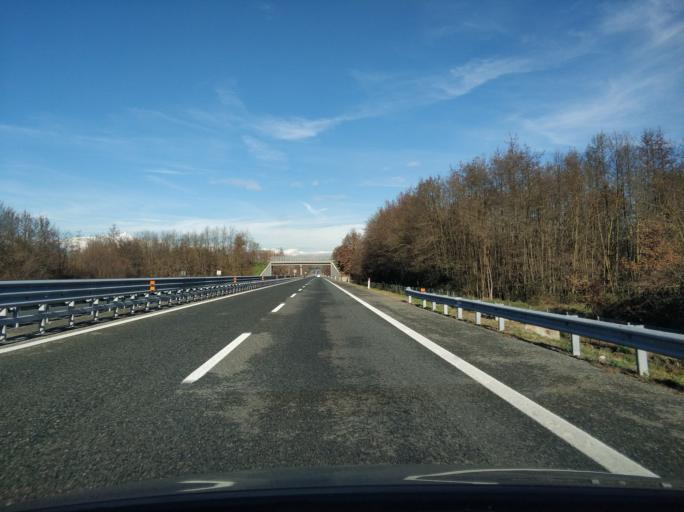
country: IT
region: Piedmont
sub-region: Provincia di Torino
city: Foglizzo
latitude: 45.2857
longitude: 7.8146
